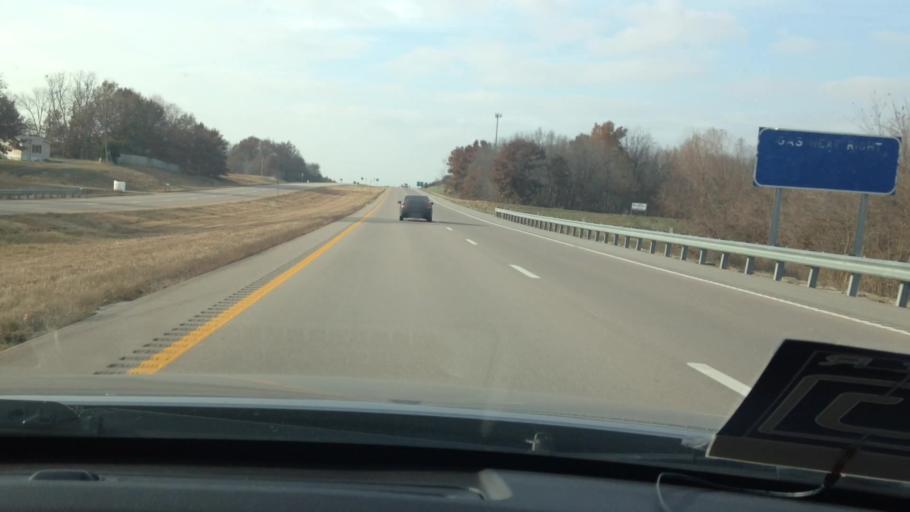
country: US
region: Missouri
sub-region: Cass County
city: Garden City
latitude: 38.4955
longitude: -94.0605
